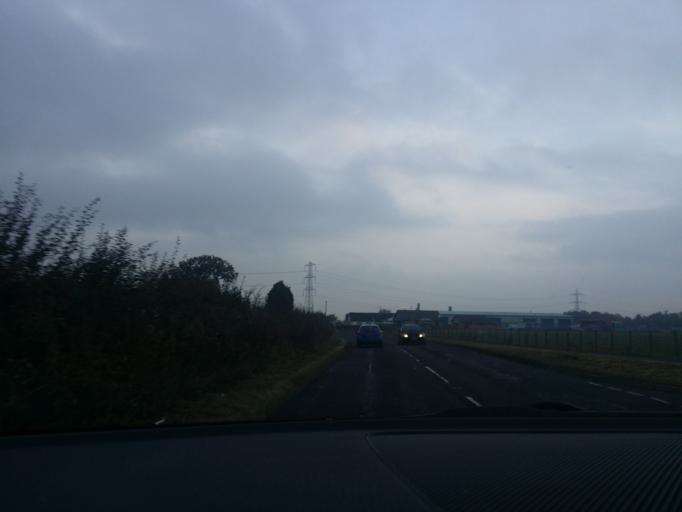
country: GB
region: Scotland
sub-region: Falkirk
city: Airth
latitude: 56.0569
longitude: -3.7604
